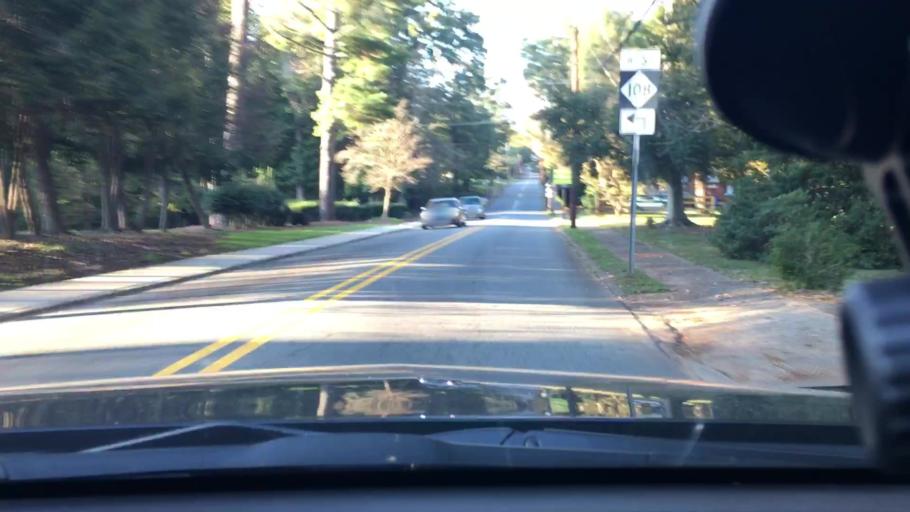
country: US
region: North Carolina
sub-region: Rutherford County
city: Rutherfordton
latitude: 35.3639
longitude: -81.9653
